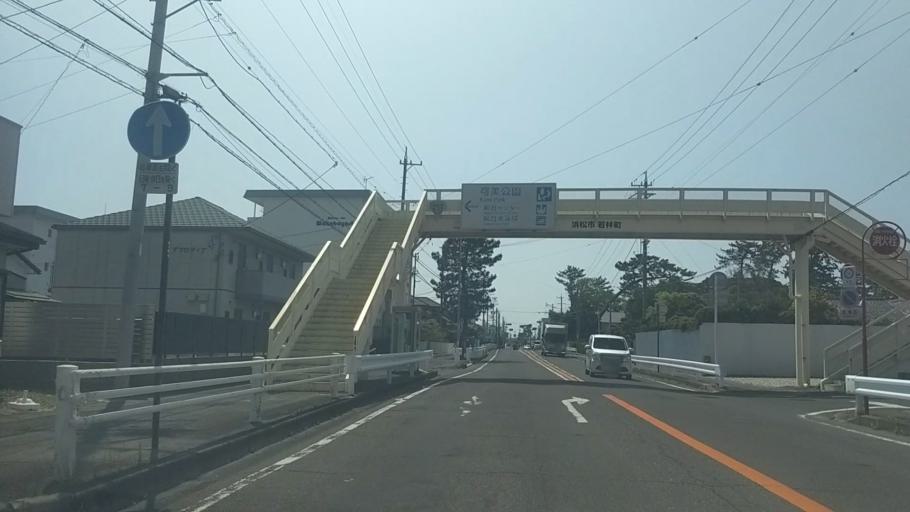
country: JP
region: Shizuoka
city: Hamamatsu
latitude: 34.6885
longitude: 137.6970
